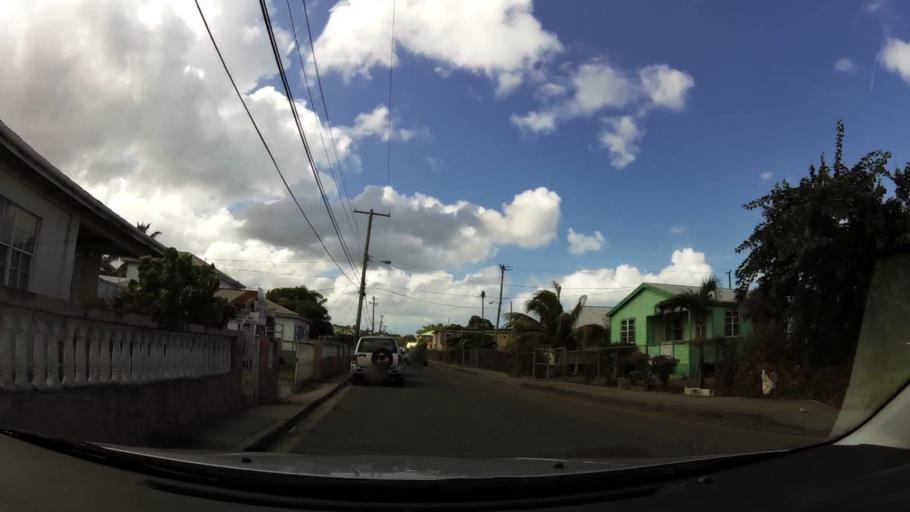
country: AG
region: Saint John
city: Saint John's
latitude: 17.1054
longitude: -61.8374
